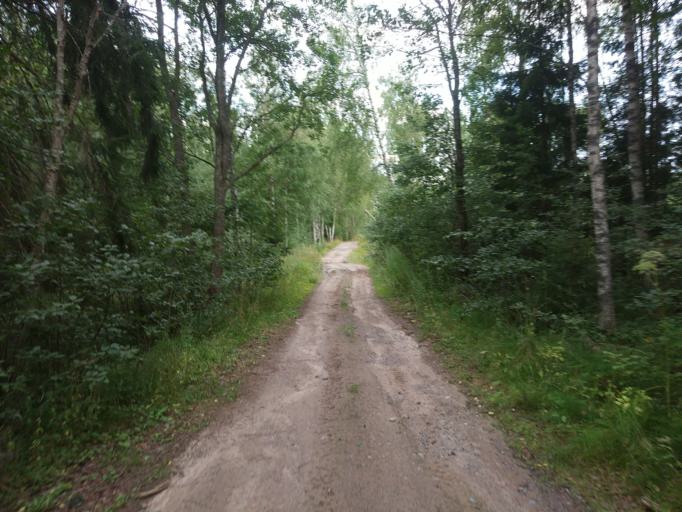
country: RU
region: Leningrad
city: Kuznechnoye
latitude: 61.1116
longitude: 29.6115
